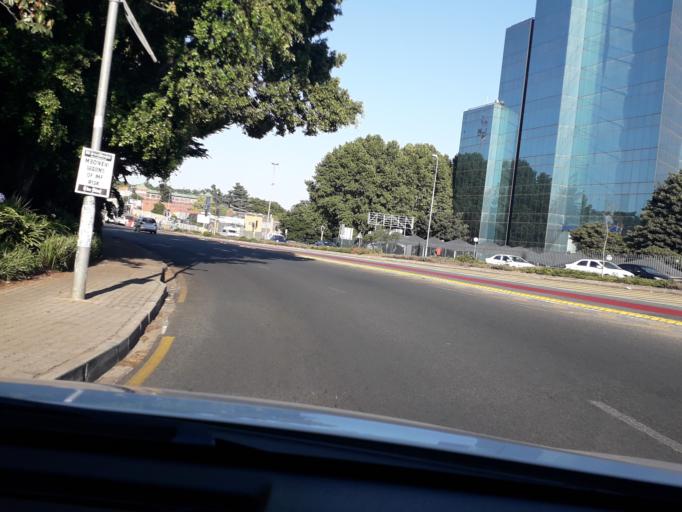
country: ZA
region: Gauteng
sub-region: City of Johannesburg Metropolitan Municipality
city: Johannesburg
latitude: -26.1831
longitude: 28.0194
